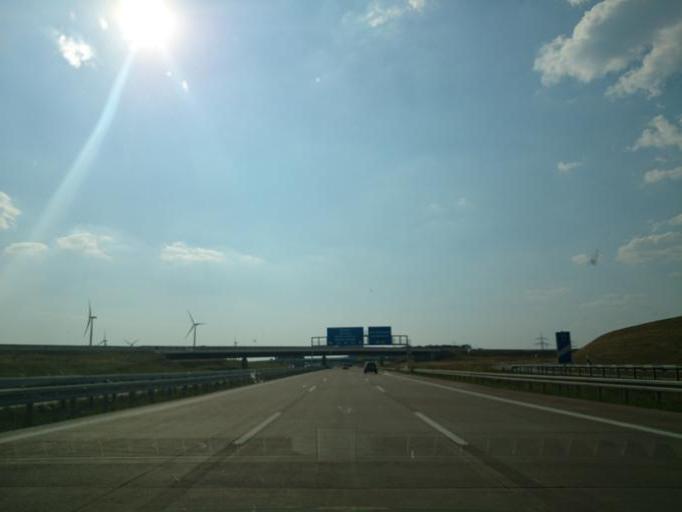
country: DE
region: Brandenburg
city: Ahrensfelde
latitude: 52.6131
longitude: 13.5664
